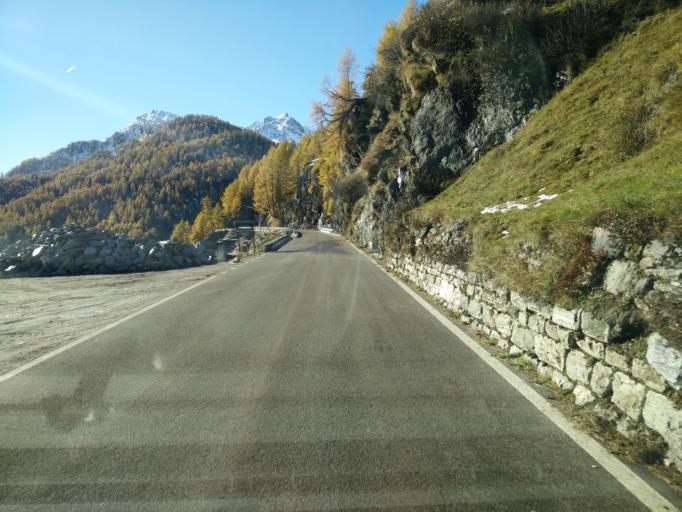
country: IT
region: Trentino-Alto Adige
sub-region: Bolzano
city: Moso in Passiria
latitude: 46.8910
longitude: 11.1273
